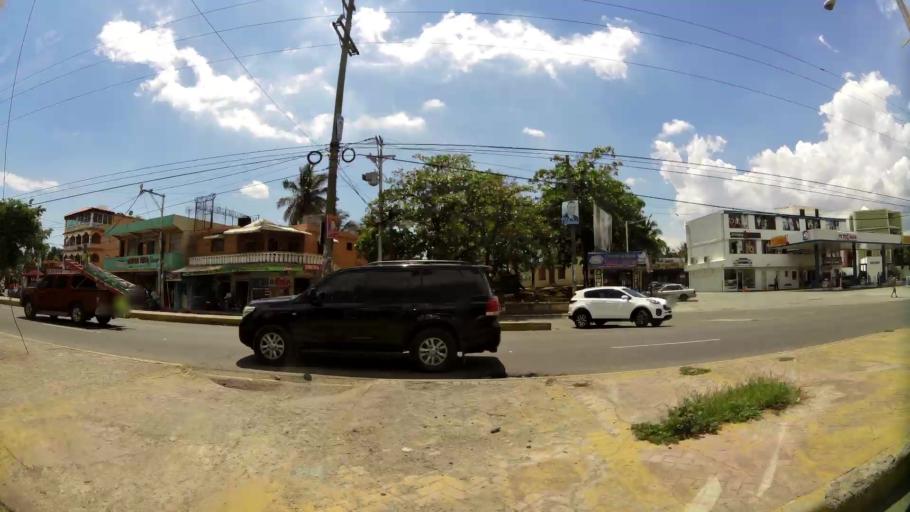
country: DO
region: Santo Domingo
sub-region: Santo Domingo
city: Santo Domingo Este
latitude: 18.5436
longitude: -69.8636
